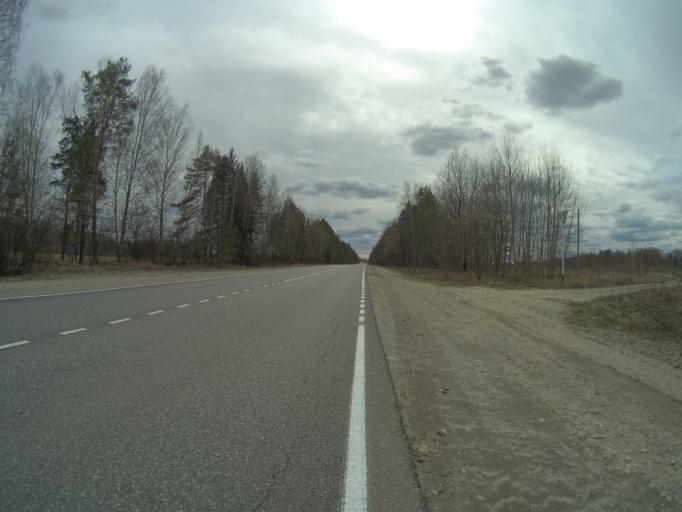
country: RU
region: Vladimir
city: Golovino
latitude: 55.9963
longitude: 40.5622
